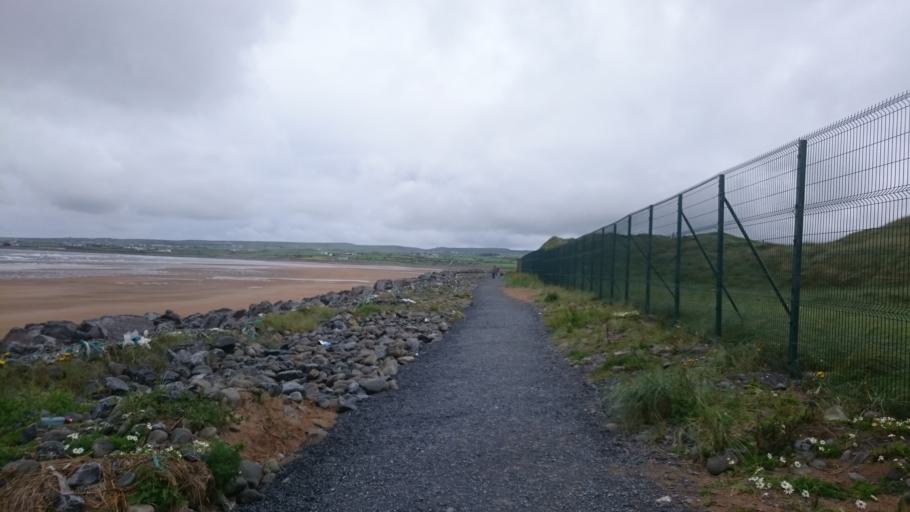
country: IE
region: Munster
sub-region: An Clar
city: Kilrush
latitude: 52.9373
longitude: -9.3537
